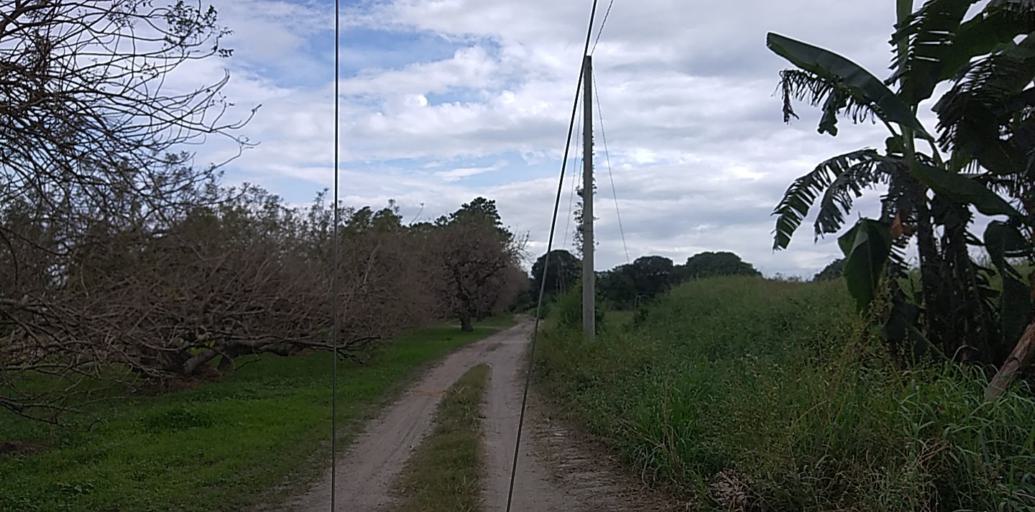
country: PH
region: Central Luzon
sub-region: Province of Pampanga
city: Pulung Santol
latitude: 15.0374
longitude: 120.5601
